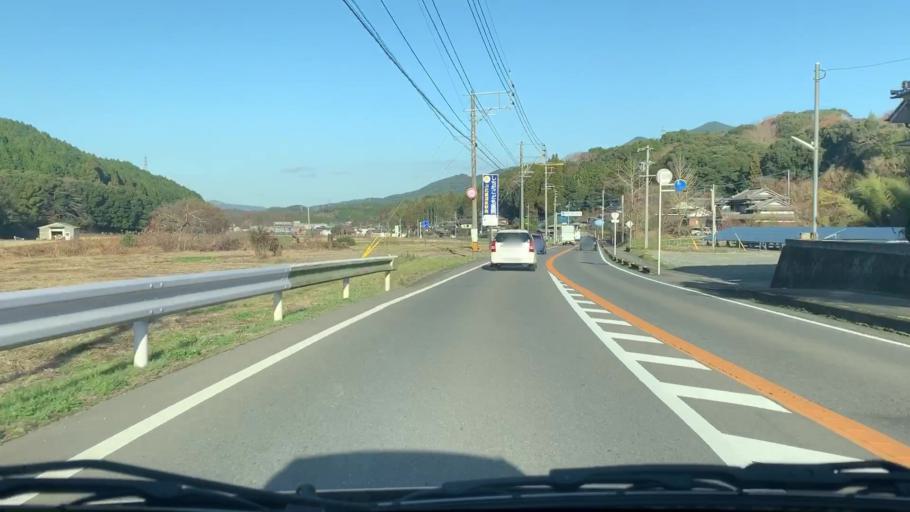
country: JP
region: Saga Prefecture
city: Takeocho-takeo
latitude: 33.2457
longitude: 130.0053
